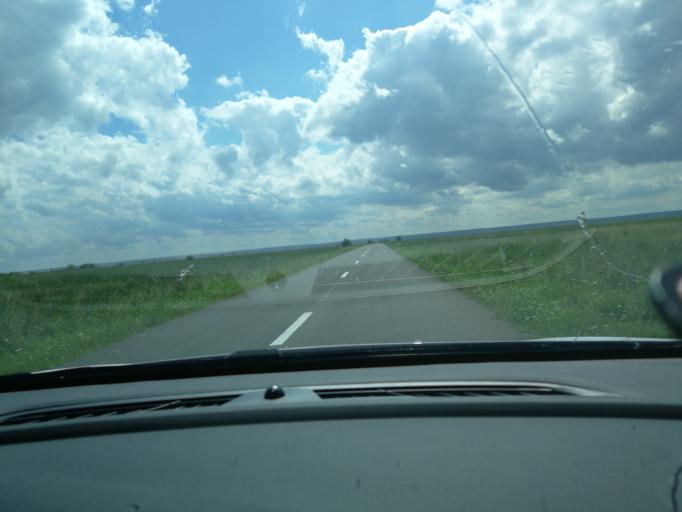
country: RO
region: Constanta
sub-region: Comuna Istria
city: Istria
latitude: 44.5442
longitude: 28.7674
